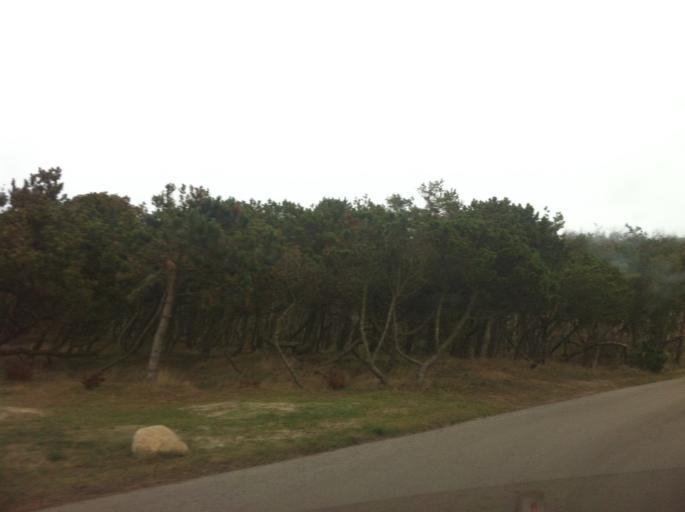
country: SE
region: Skane
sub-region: Hoganas Kommun
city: Hoganas
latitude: 56.1806
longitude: 12.5560
